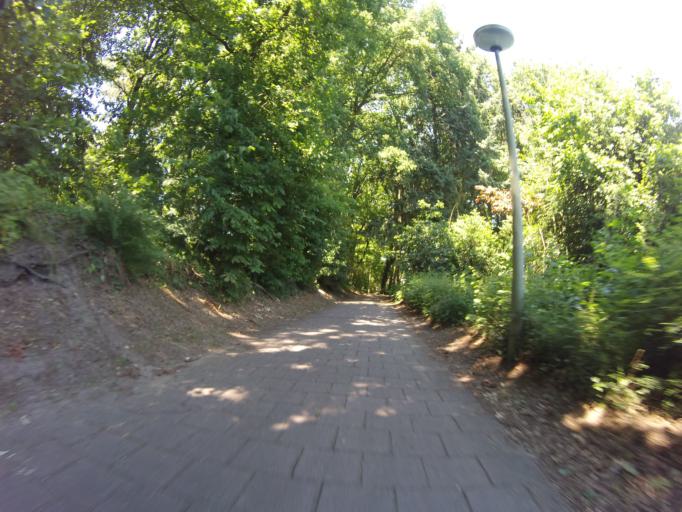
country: NL
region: Drenthe
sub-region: Gemeente Emmen
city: Emmen
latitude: 52.7868
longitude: 6.9305
